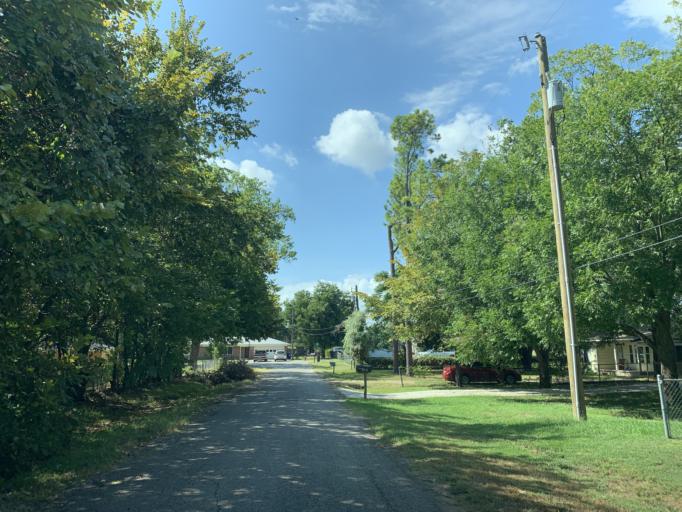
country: US
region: Texas
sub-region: Tarrant County
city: Azle
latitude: 32.8810
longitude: -97.5401
